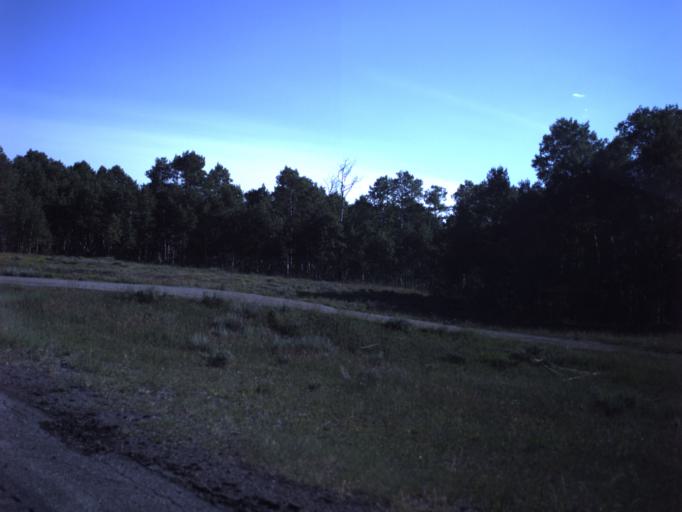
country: US
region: Utah
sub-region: Sanpete County
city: Fairview
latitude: 39.6601
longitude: -111.3282
